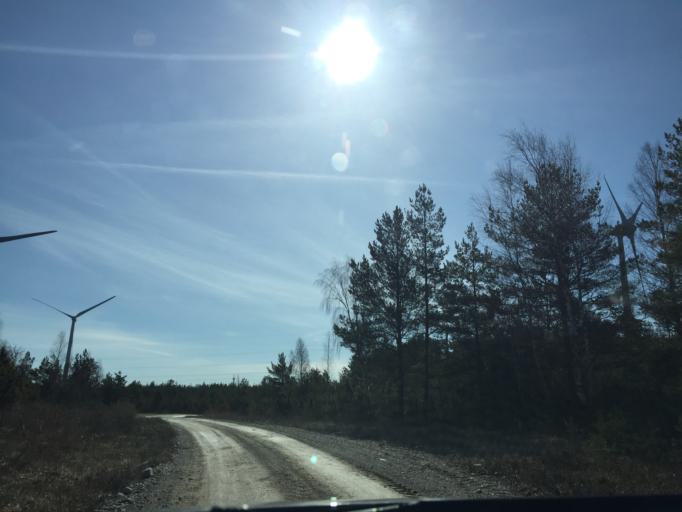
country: EE
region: Laeaene
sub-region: Haapsalu linn
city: Haapsalu
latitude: 58.6355
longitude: 23.5229
